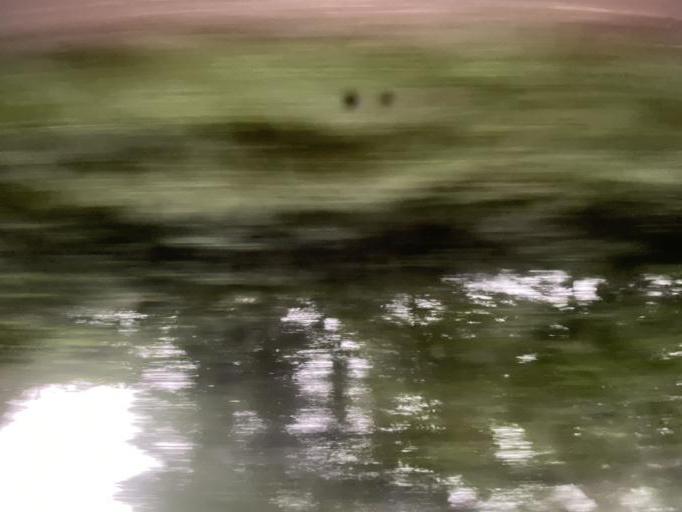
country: US
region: Indiana
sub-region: LaPorte County
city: Westville
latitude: 41.5995
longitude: -86.8922
